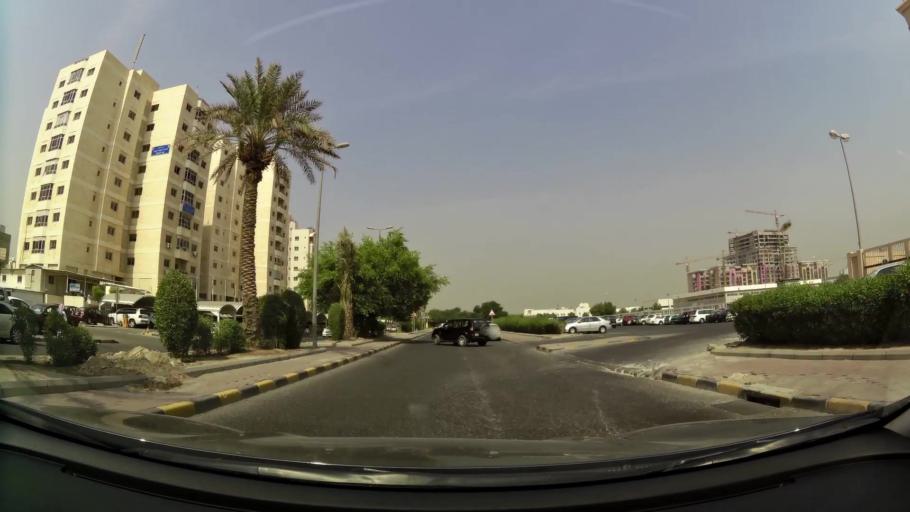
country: KW
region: Al Asimah
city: Ar Rabiyah
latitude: 29.3077
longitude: 47.9208
